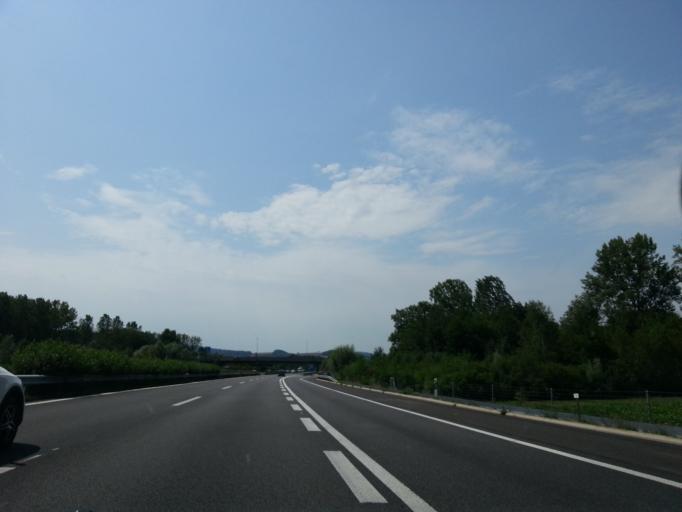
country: CH
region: Vaud
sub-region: Broye-Vully District
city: Payerne
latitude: 46.8292
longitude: 6.9111
